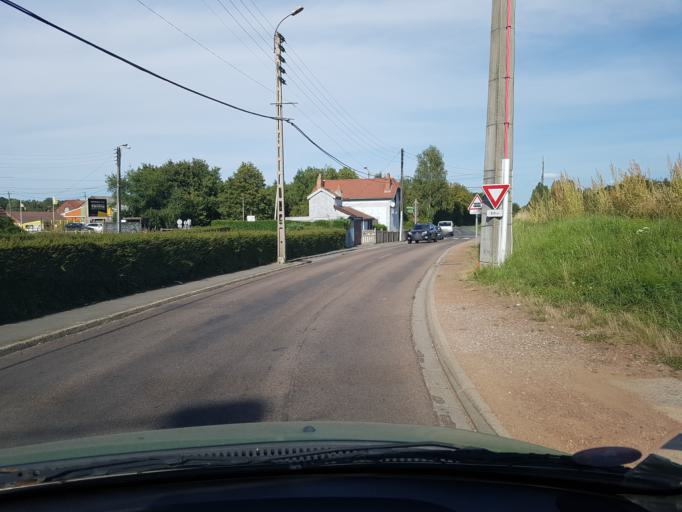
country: FR
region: Nord-Pas-de-Calais
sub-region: Departement du Pas-de-Calais
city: Lapugnoy
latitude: 50.5090
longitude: 2.5251
